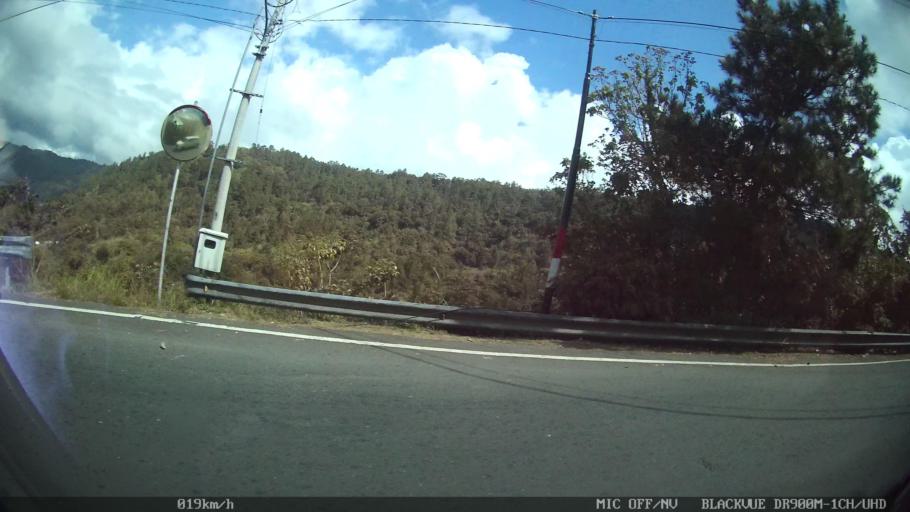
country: ID
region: Bali
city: Banjar Kedisan
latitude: -8.2804
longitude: 115.3709
